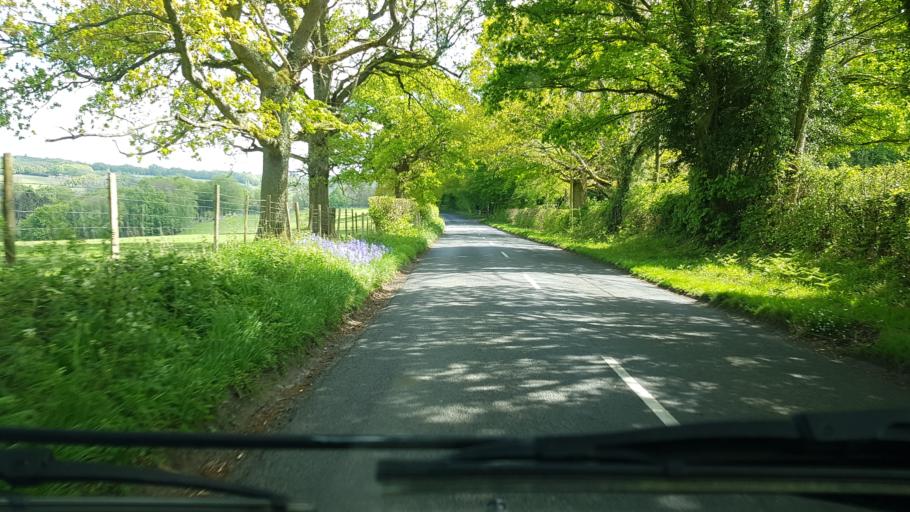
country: GB
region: England
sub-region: East Sussex
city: Robertsbridge
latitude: 51.0347
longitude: 0.4370
